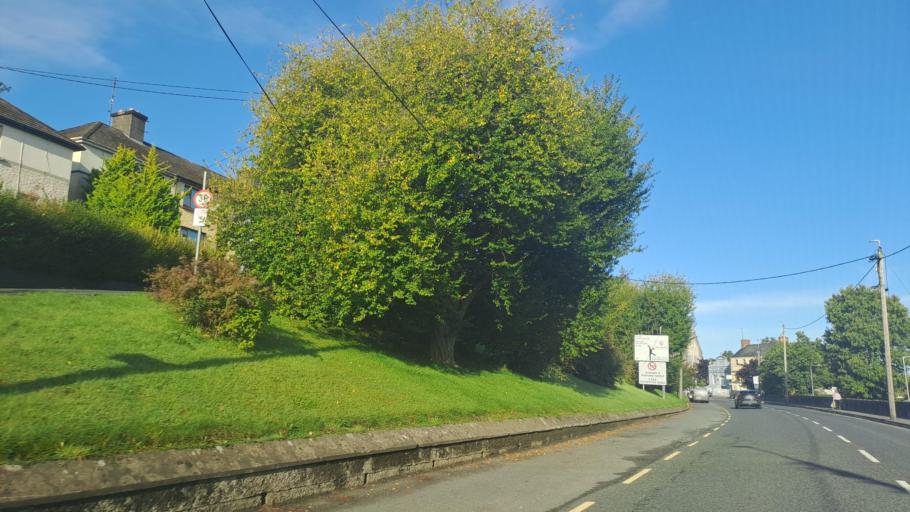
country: IE
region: Ulster
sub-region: County Monaghan
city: Carrickmacross
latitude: 53.9753
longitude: -6.7120
